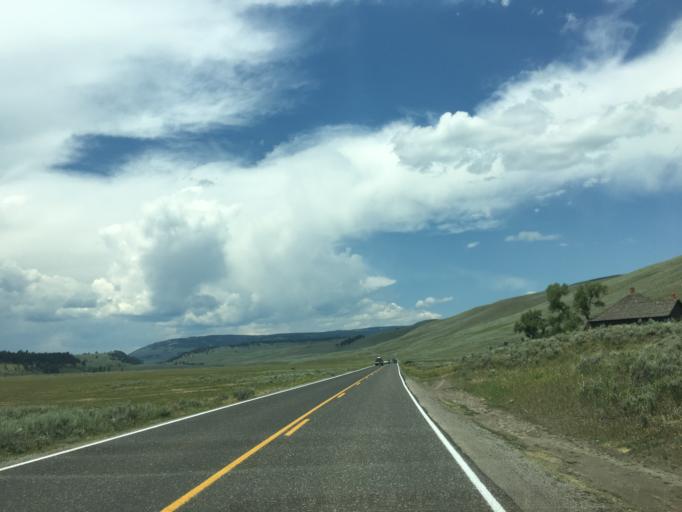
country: US
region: Montana
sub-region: Park County
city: Livingston
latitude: 44.8945
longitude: -110.2354
